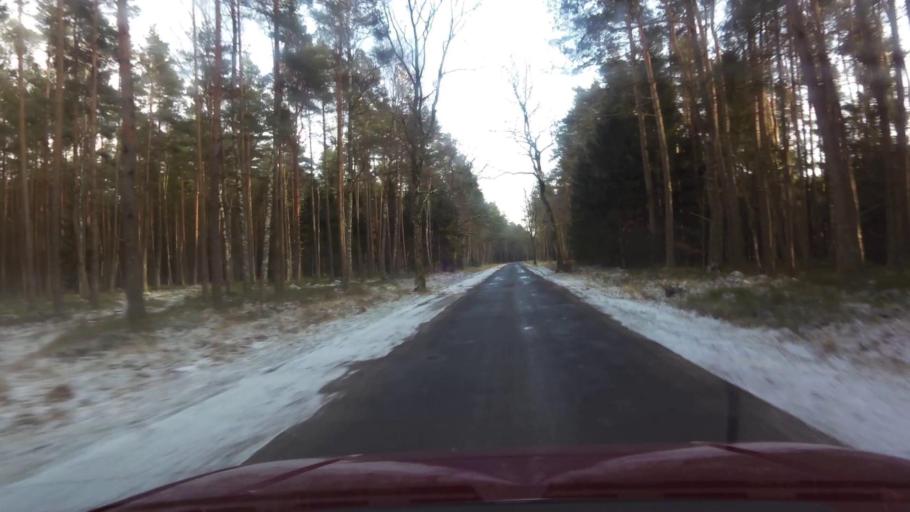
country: PL
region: West Pomeranian Voivodeship
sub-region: Powiat bialogardzki
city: Bialogard
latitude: 54.1027
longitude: 16.0355
